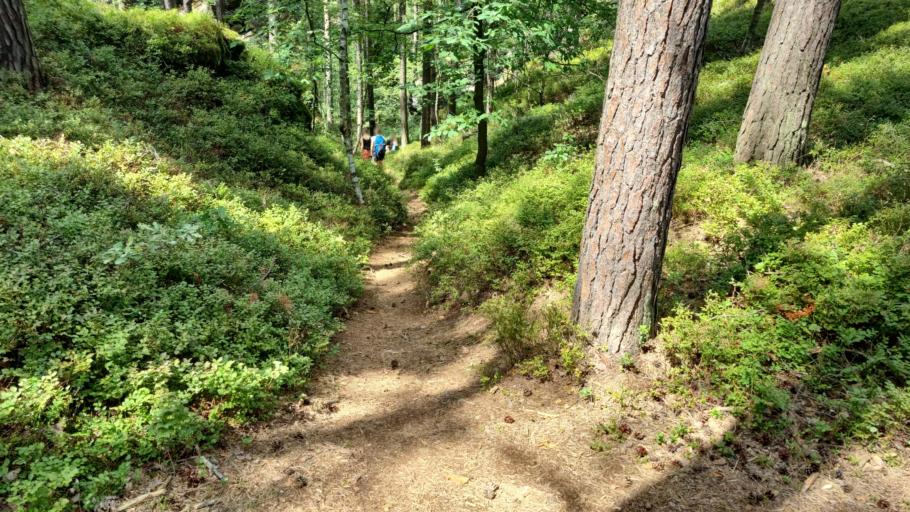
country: CZ
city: Cvikov
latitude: 50.7827
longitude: 14.6721
